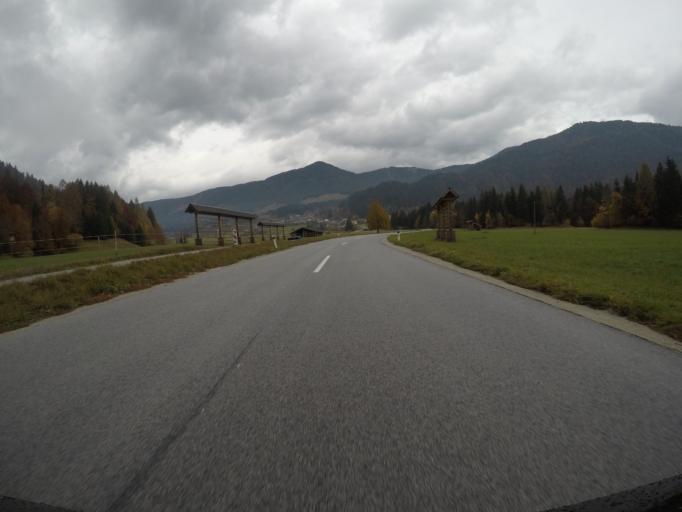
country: AT
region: Carinthia
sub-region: Politischer Bezirk Villach Land
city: Arnoldstein
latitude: 46.4878
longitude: 13.7242
